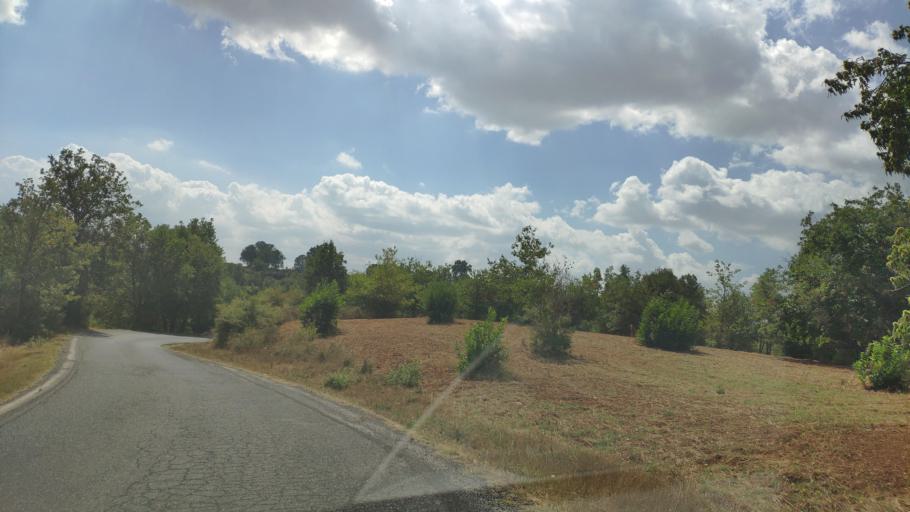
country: GR
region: Peloponnese
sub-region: Nomos Lakonias
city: Kariai
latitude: 37.3222
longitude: 22.4287
